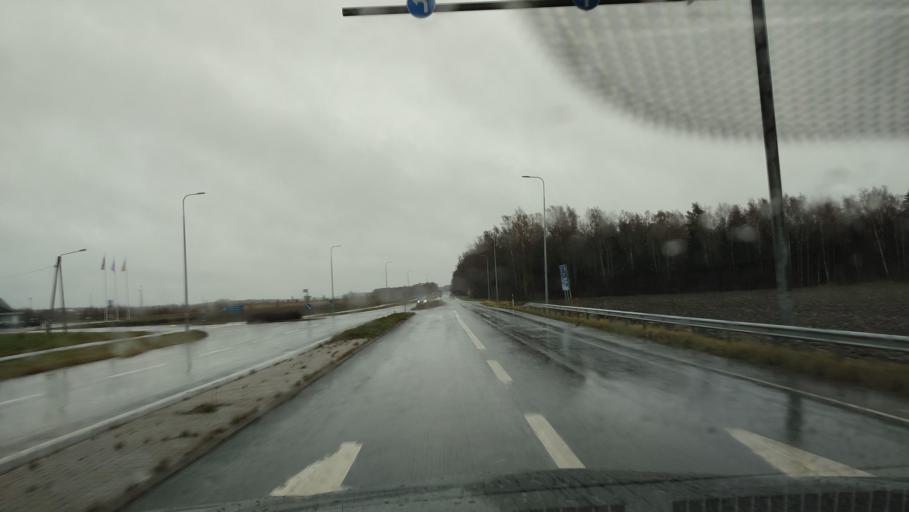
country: FI
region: Ostrobothnia
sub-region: Vaasa
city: Ristinummi
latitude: 63.0487
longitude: 21.7285
